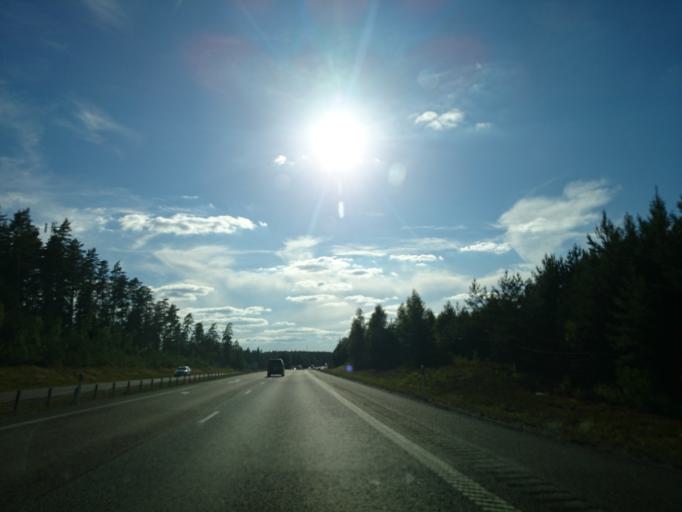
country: SE
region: Soedermanland
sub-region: Nykopings Kommun
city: Olstorp
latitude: 58.7545
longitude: 16.5935
